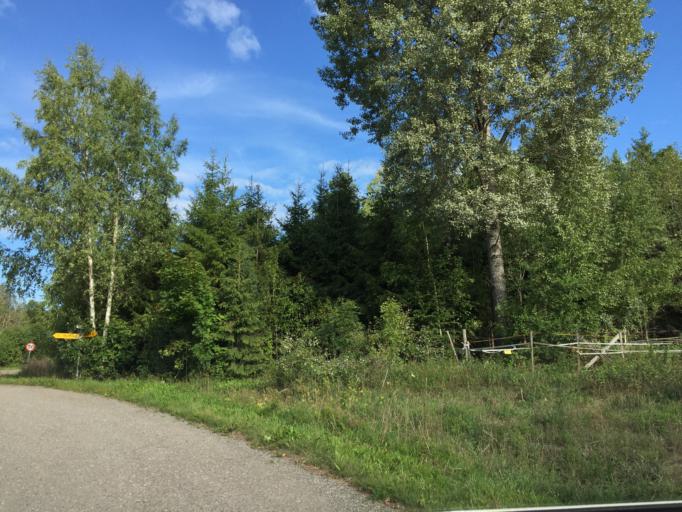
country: NO
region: Vestfold
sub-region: Holmestrand
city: Gullhaug
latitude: 59.4747
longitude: 10.1869
